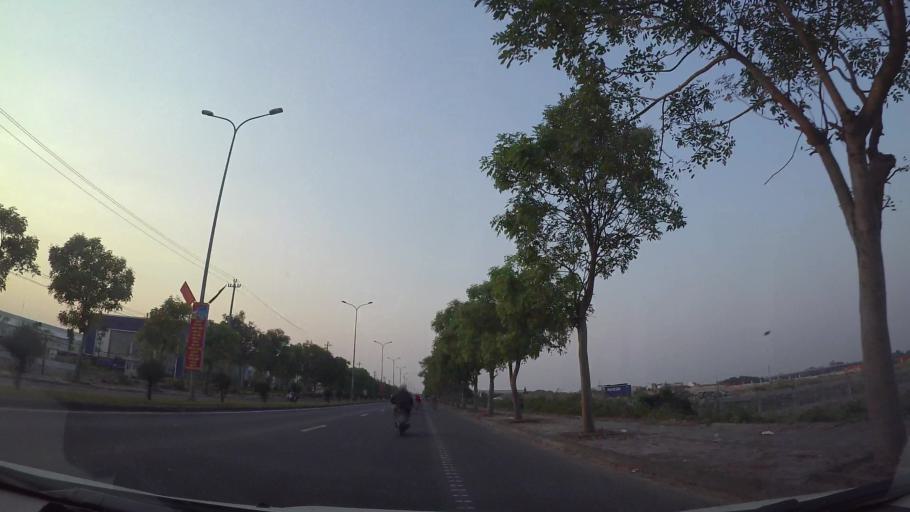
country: VN
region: Da Nang
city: Cam Le
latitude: 15.9625
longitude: 108.2131
